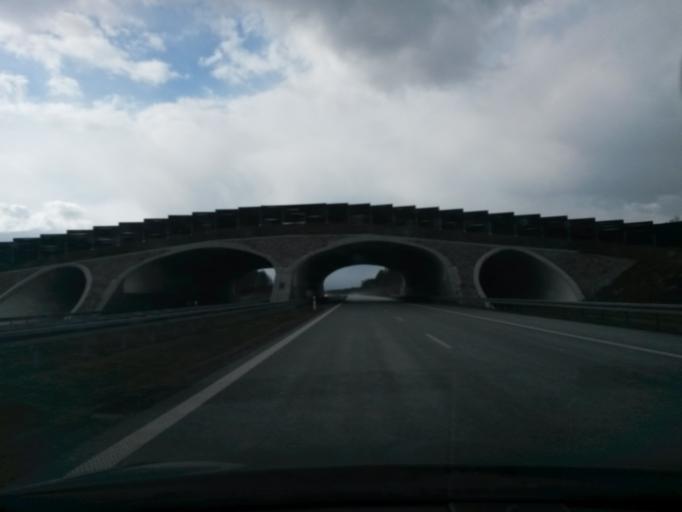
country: PL
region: Greater Poland Voivodeship
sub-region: Powiat turecki
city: Tuliszkow
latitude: 52.1446
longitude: 18.3224
